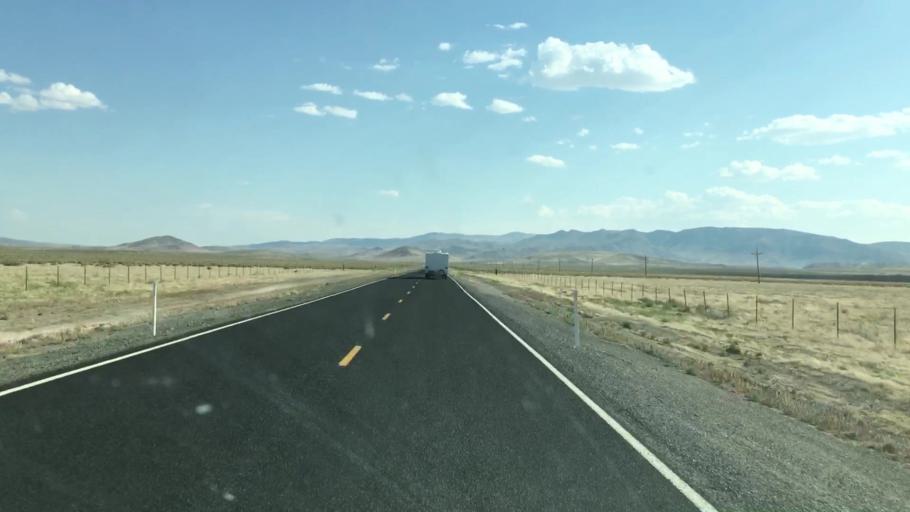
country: US
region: Nevada
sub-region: Lyon County
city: Fernley
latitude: 39.6778
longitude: -119.3336
